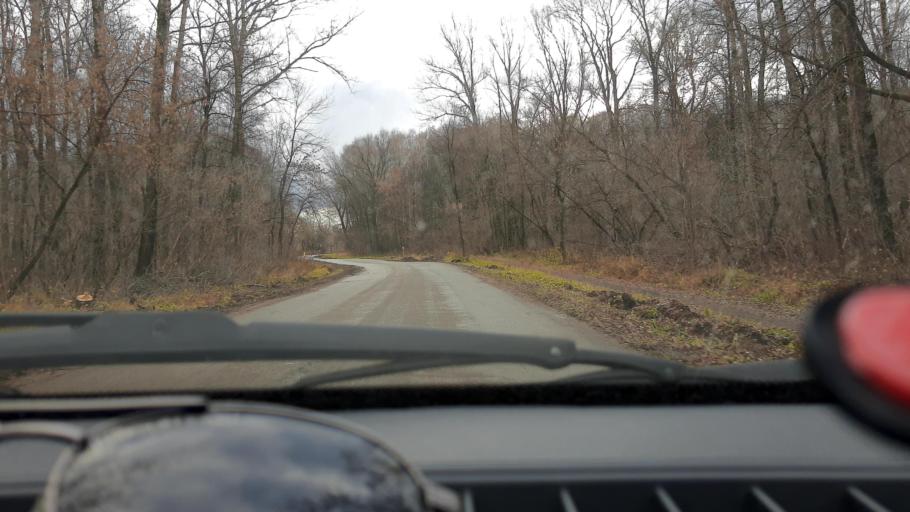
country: RU
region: Bashkortostan
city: Ufa
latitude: 54.7937
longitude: 56.1549
